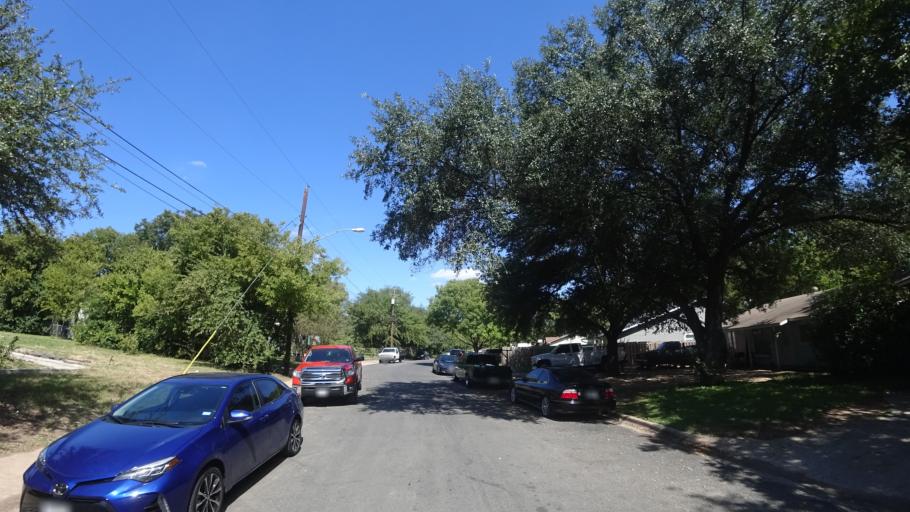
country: US
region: Texas
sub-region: Travis County
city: Austin
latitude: 30.3157
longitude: -97.6900
